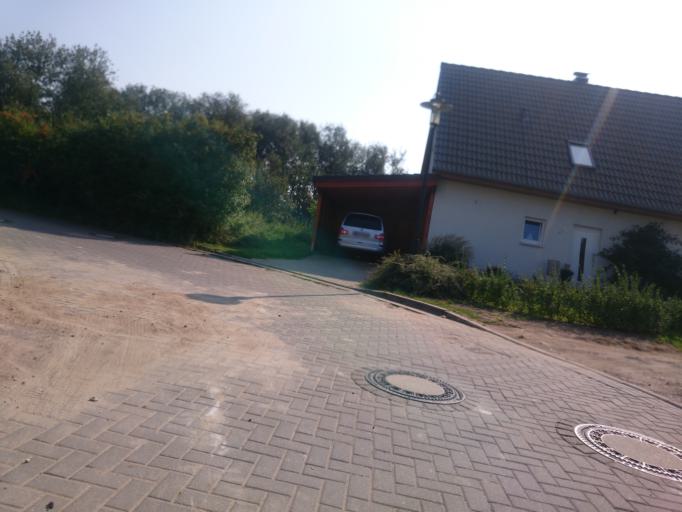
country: DE
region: Mecklenburg-Vorpommern
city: Barth
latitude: 54.3569
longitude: 12.7130
